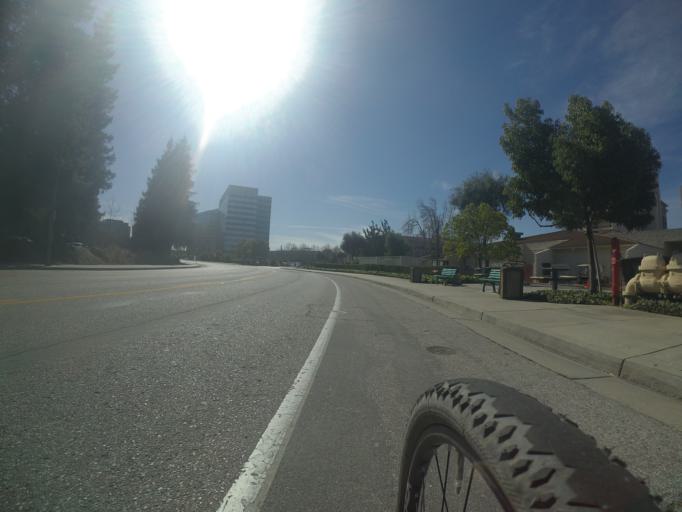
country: US
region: California
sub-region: Santa Clara County
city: Santa Clara
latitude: 37.3903
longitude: -121.9731
